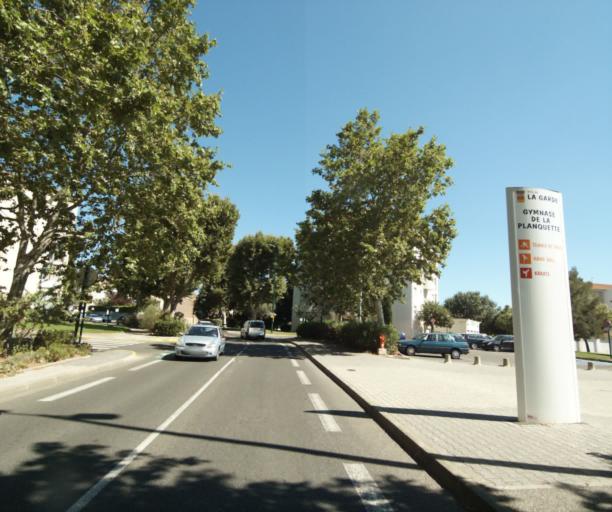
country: FR
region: Provence-Alpes-Cote d'Azur
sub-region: Departement du Var
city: La Garde
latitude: 43.1290
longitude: 6.0177
